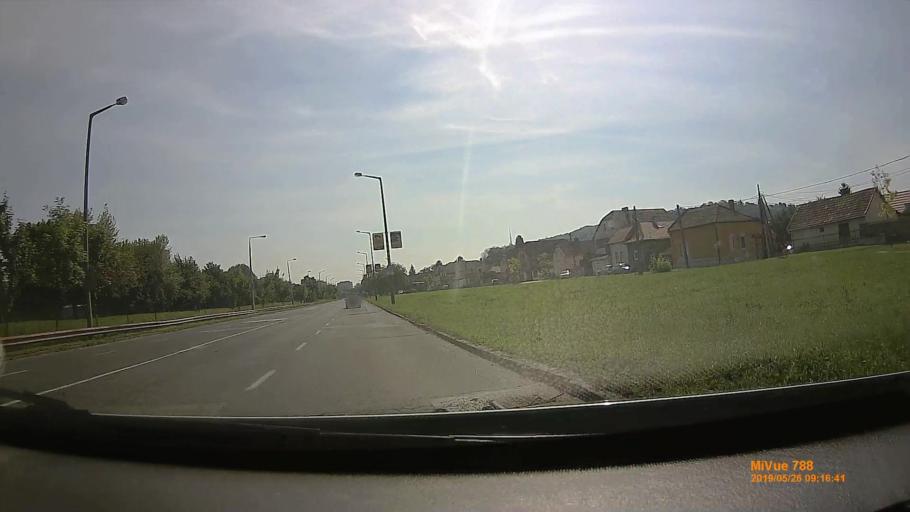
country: HU
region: Borsod-Abauj-Zemplen
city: Miskolc
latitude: 48.0998
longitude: 20.7544
